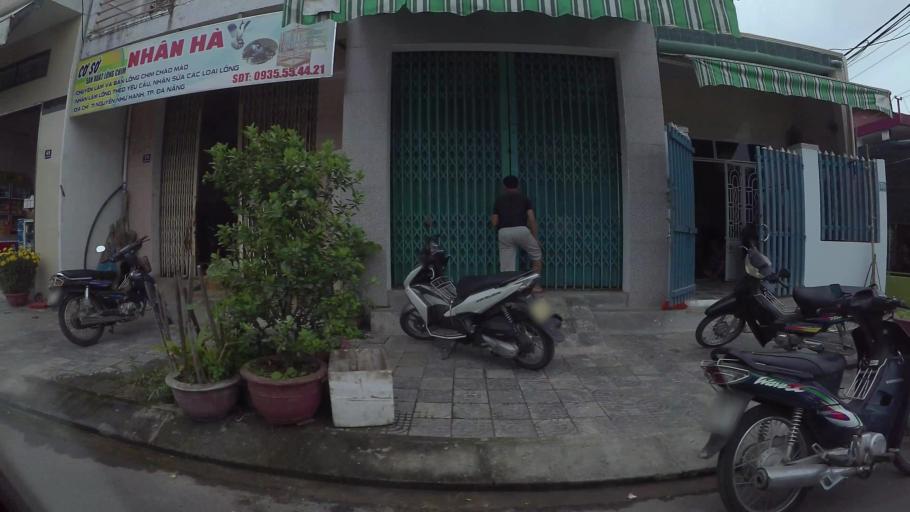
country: VN
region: Da Nang
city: Thanh Khe
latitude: 16.0630
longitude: 108.1757
